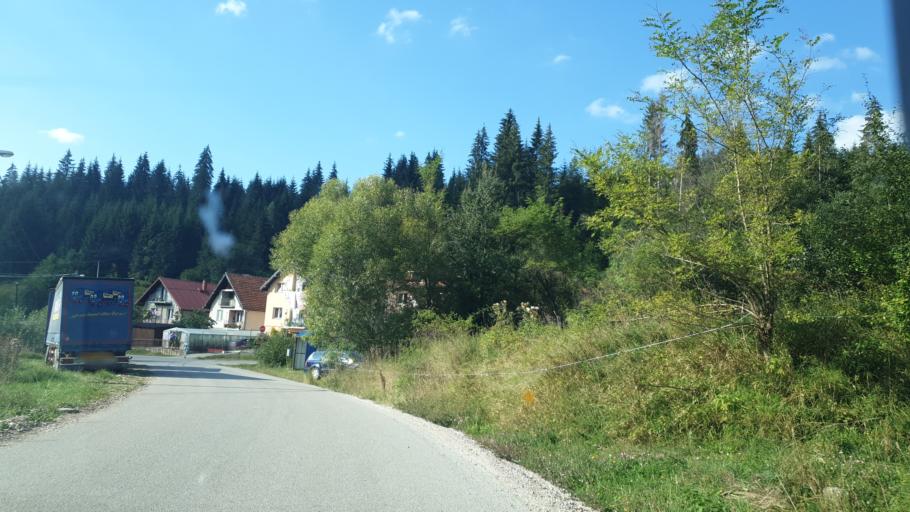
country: RS
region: Central Serbia
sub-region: Zlatiborski Okrug
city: Nova Varos
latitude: 43.4492
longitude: 19.8489
